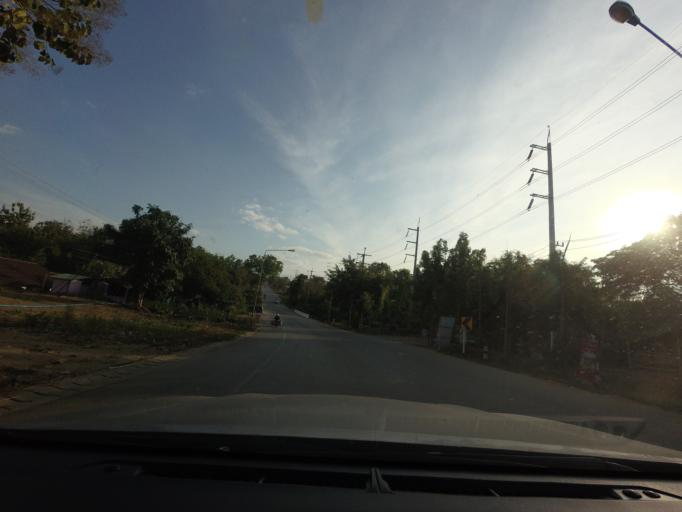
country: TH
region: Mae Hong Son
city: Mae Hi
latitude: 19.3450
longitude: 98.4328
